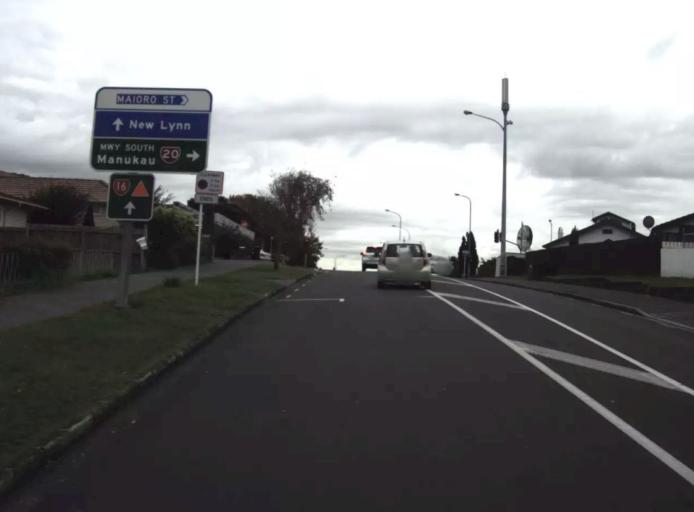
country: NZ
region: Auckland
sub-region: Auckland
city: Rosebank
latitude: -36.9079
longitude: 174.7142
